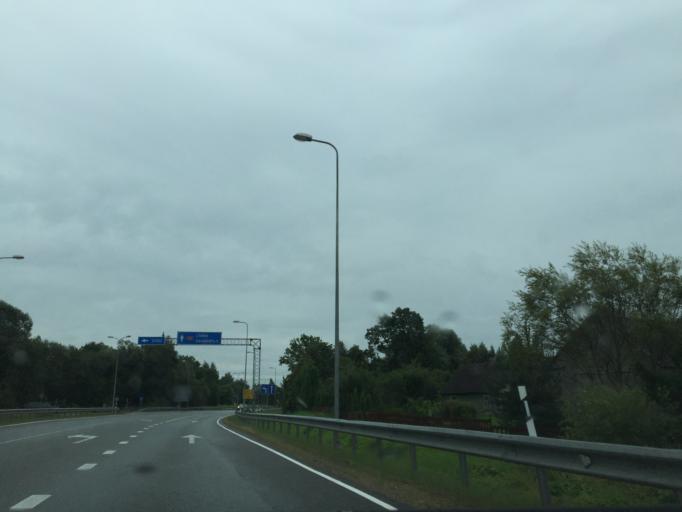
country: LV
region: Livani
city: Livani
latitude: 56.3902
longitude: 26.1507
